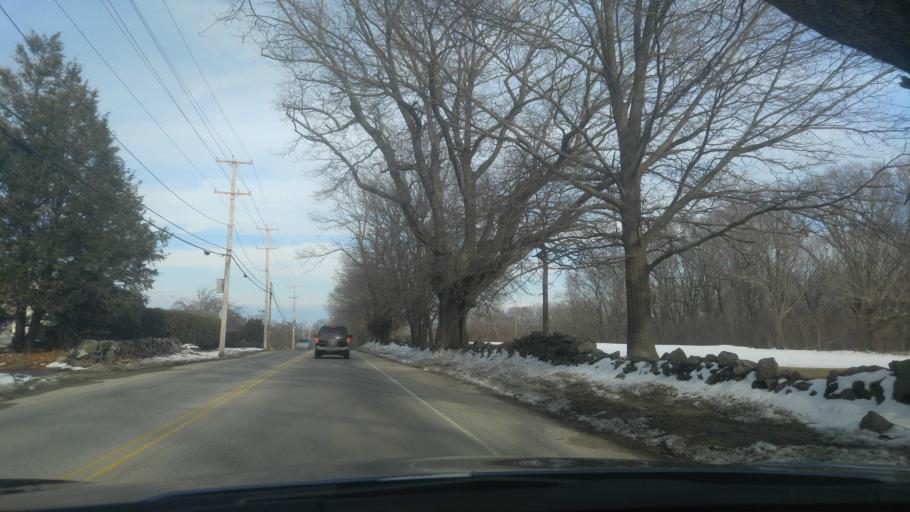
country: US
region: Rhode Island
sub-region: Kent County
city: West Warwick
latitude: 41.7079
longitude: -71.5104
